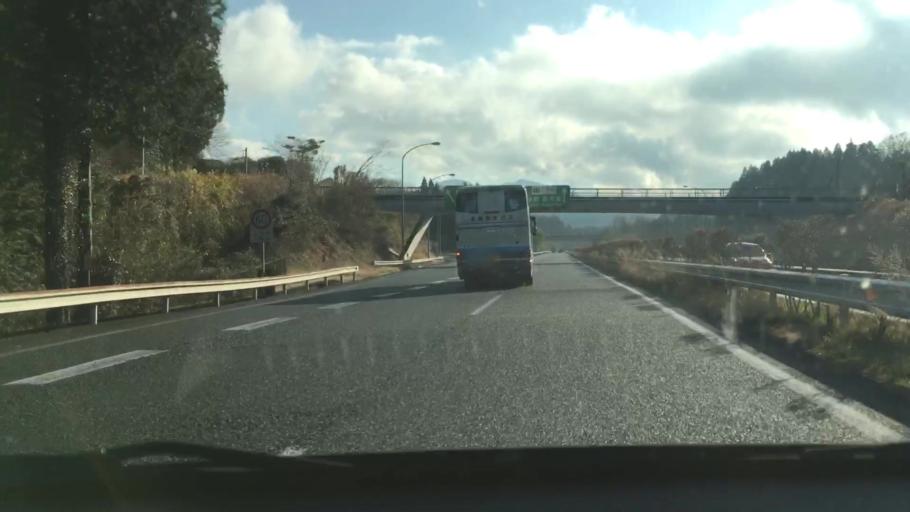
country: JP
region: Kagoshima
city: Okuchi-shinohara
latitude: 32.0366
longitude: 130.7989
